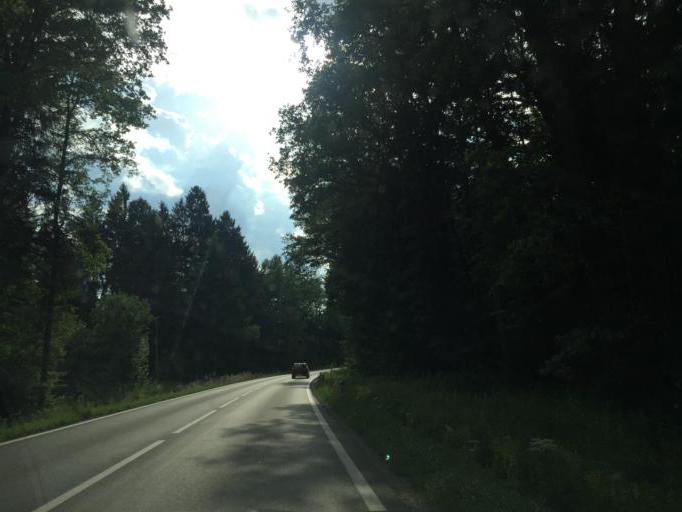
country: AT
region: Styria
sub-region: Politischer Bezirk Leibnitz
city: Sankt Veit am Vogau
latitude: 46.7576
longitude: 15.6306
